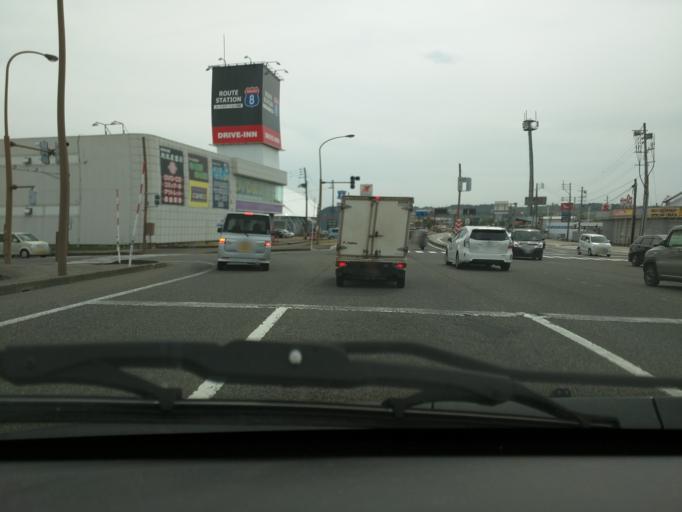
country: JP
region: Niigata
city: Nagaoka
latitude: 37.4476
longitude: 138.7985
